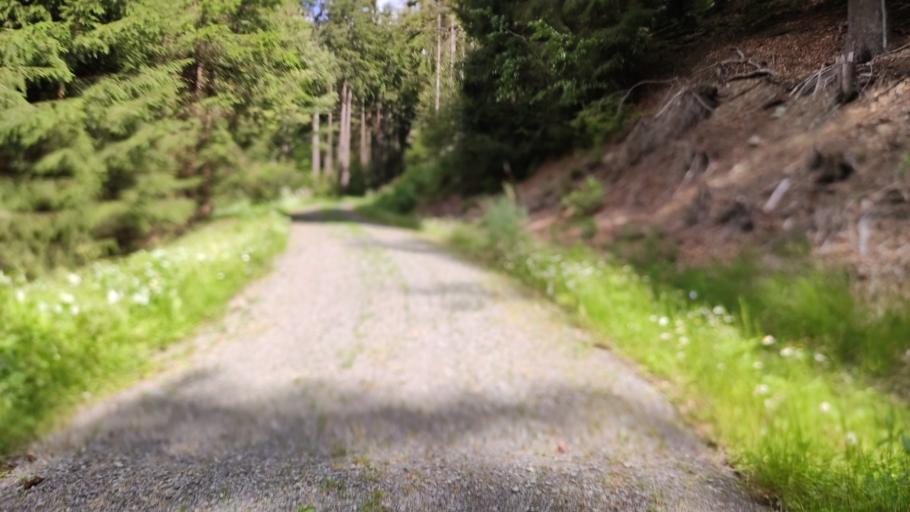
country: DE
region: Bavaria
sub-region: Upper Franconia
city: Tschirn
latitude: 50.3791
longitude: 11.4670
